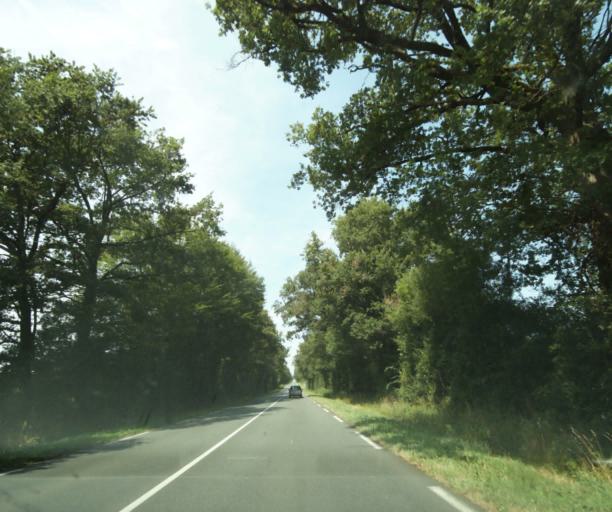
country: FR
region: Limousin
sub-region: Departement de la Haute-Vienne
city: Bussiere-Poitevine
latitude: 46.2780
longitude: 0.8569
